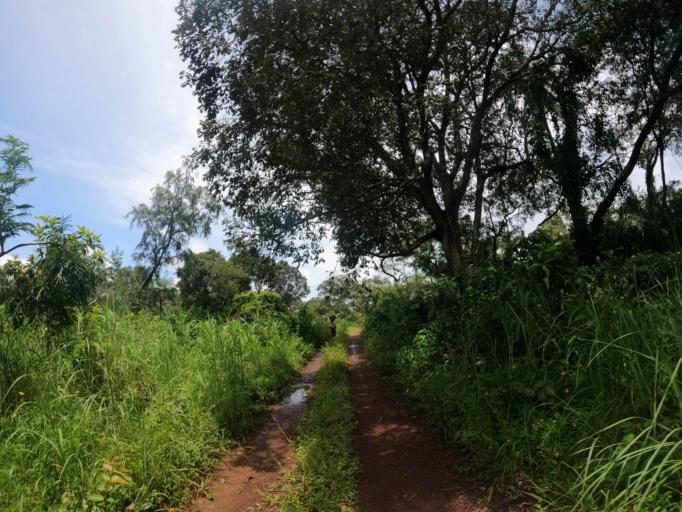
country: SL
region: Northern Province
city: Binkolo
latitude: 9.1545
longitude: -12.1969
